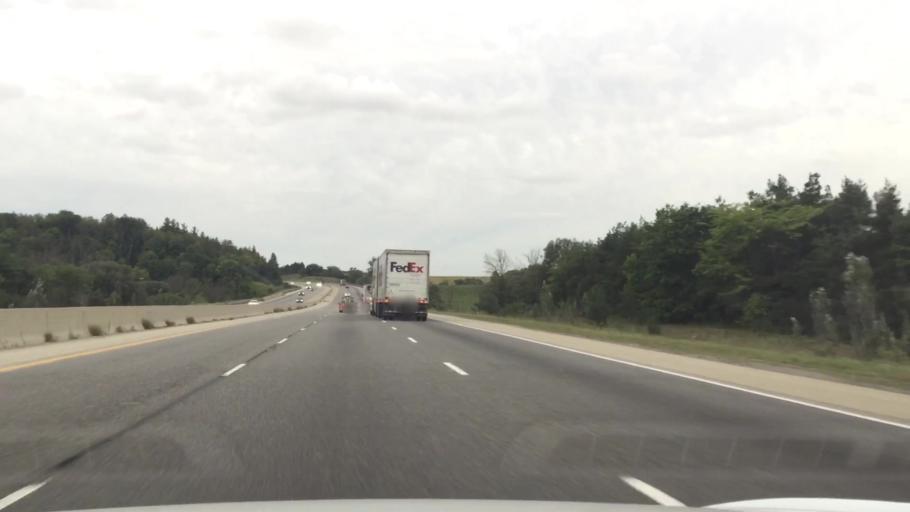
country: CA
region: Ontario
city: Kitchener
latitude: 43.2965
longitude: -80.4913
